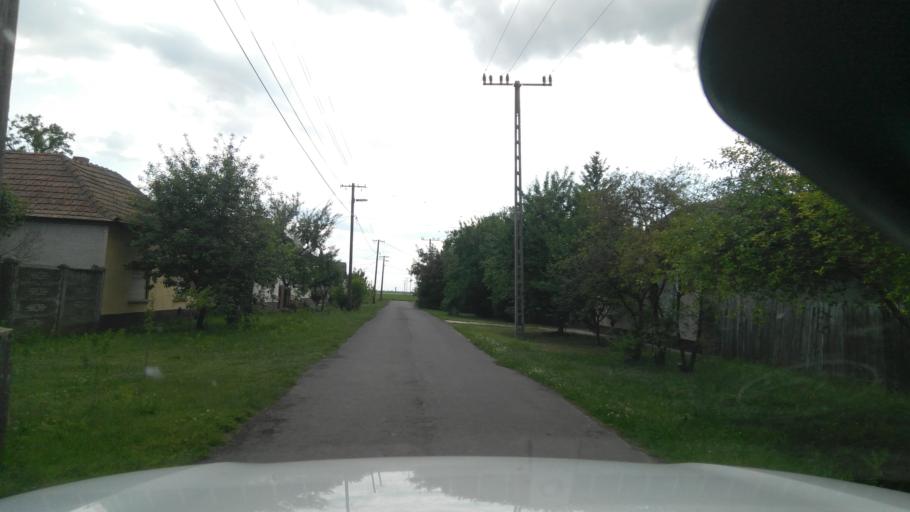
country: HU
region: Bekes
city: Magyarbanhegyes
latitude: 46.4488
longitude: 20.9724
